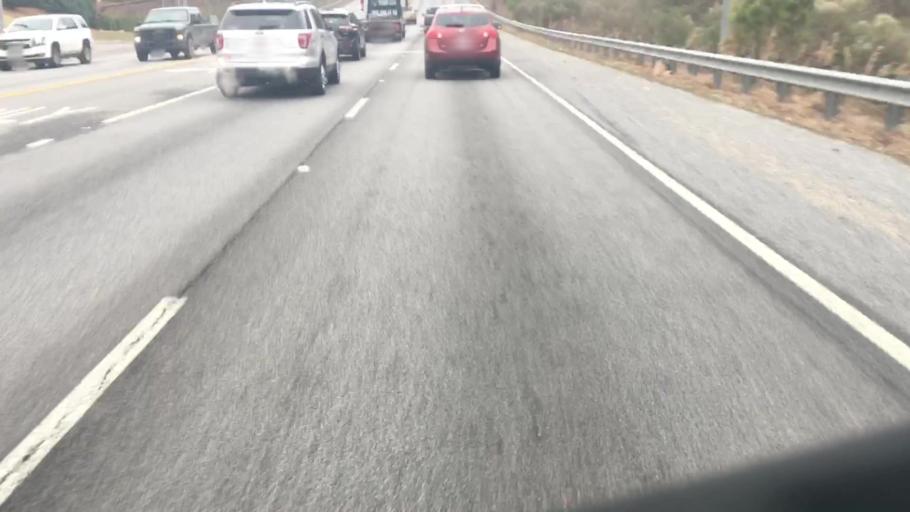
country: US
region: Alabama
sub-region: Shelby County
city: Helena
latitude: 33.3531
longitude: -86.8627
